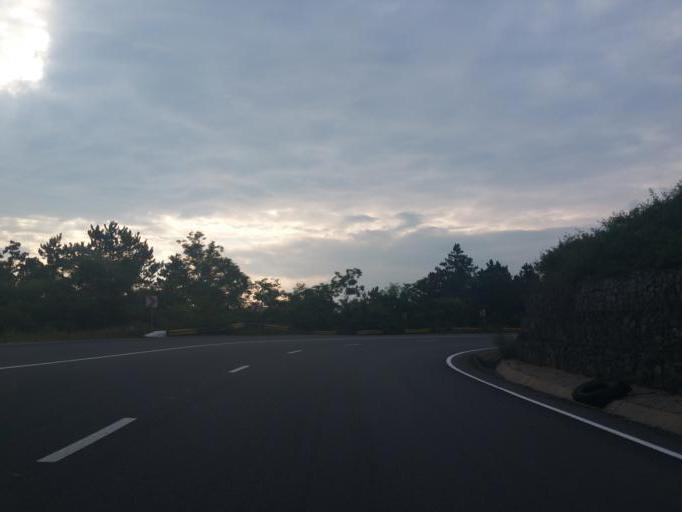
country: RO
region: Salaj
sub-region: Comuna Dragu
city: Dragu
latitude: 46.9471
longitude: 23.3708
